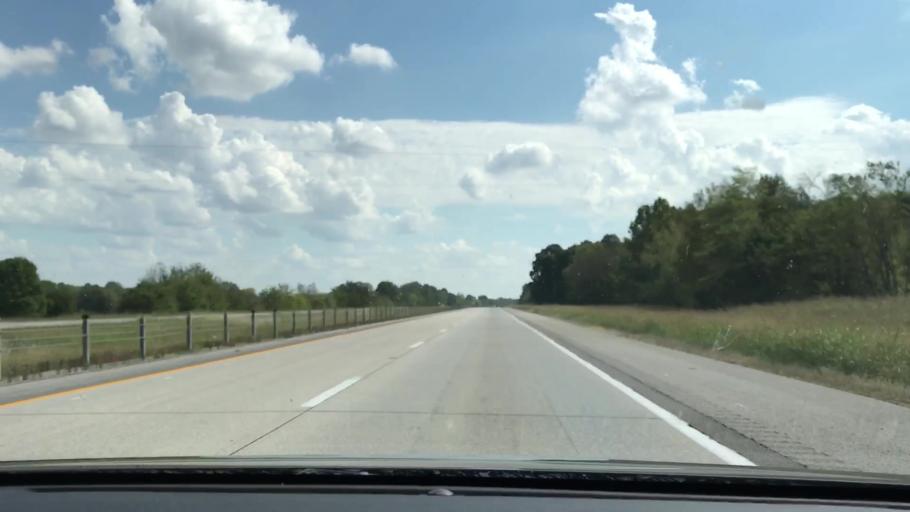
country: US
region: Kentucky
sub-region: Trigg County
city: Cadiz
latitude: 36.8487
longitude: -87.6882
